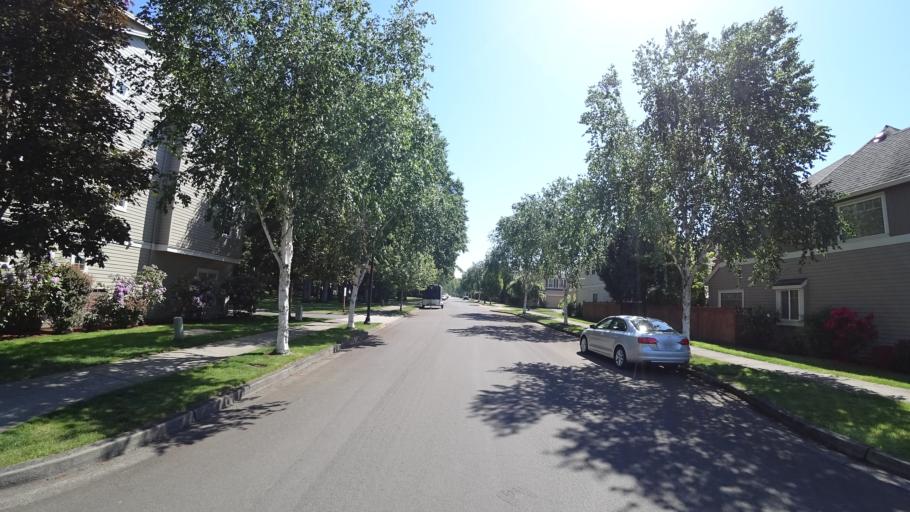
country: US
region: Oregon
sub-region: Washington County
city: Rockcreek
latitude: 45.5288
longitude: -122.9191
